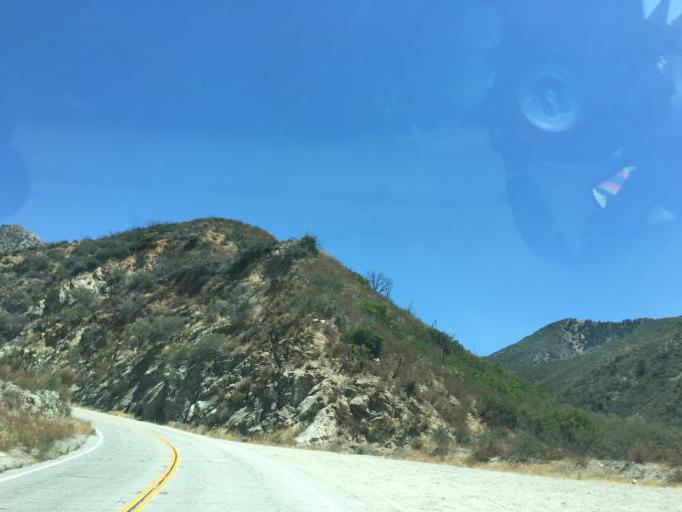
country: US
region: California
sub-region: Los Angeles County
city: La Crescenta-Montrose
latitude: 34.2832
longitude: -118.1958
